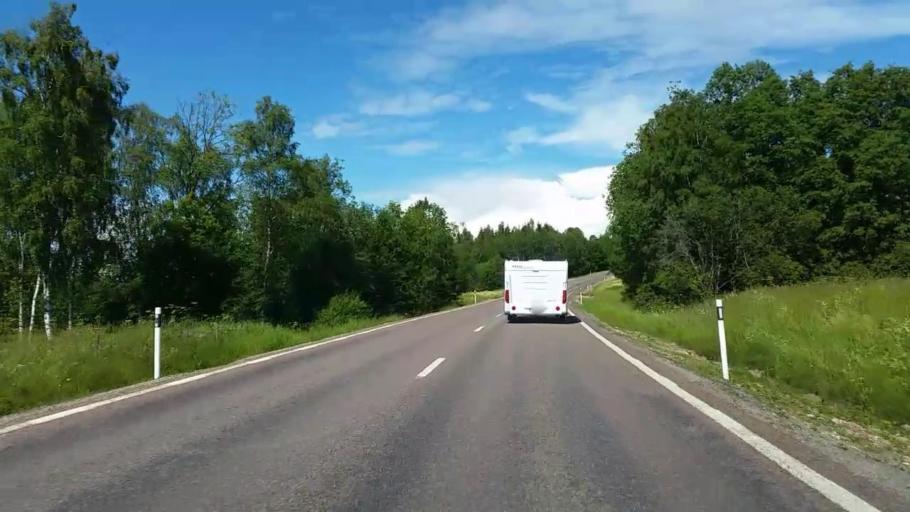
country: SE
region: Dalarna
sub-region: Rattviks Kommun
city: Raettvik
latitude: 60.9919
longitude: 15.2177
